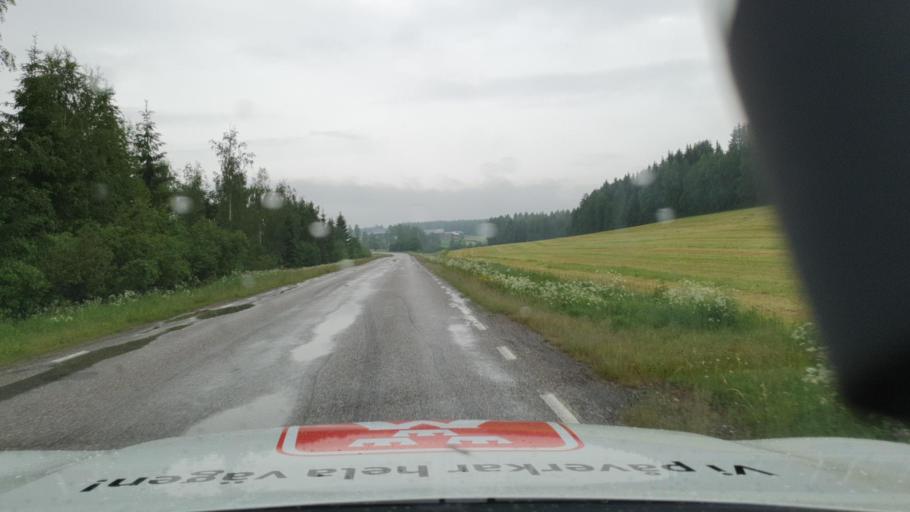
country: SE
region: Vaesterbotten
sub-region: Vannas Kommun
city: Vaennaes
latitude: 63.7869
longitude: 19.5768
